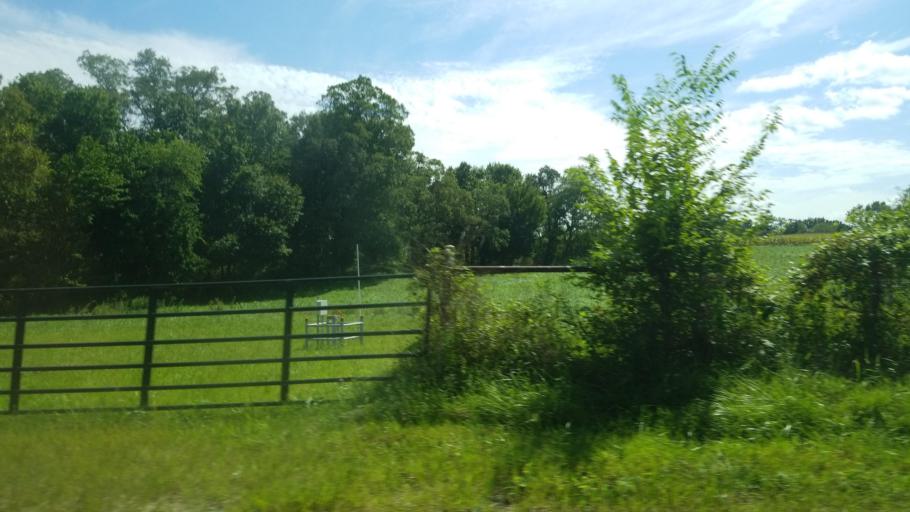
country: US
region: Illinois
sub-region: Williamson County
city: Johnston City
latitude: 37.7902
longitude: -88.8186
